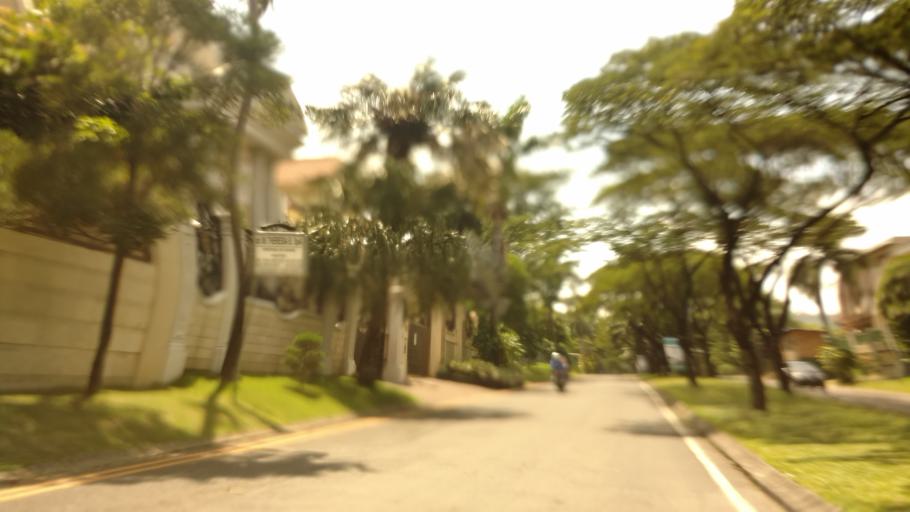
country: ID
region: East Java
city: Driyorejo
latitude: -7.2944
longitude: 112.6542
